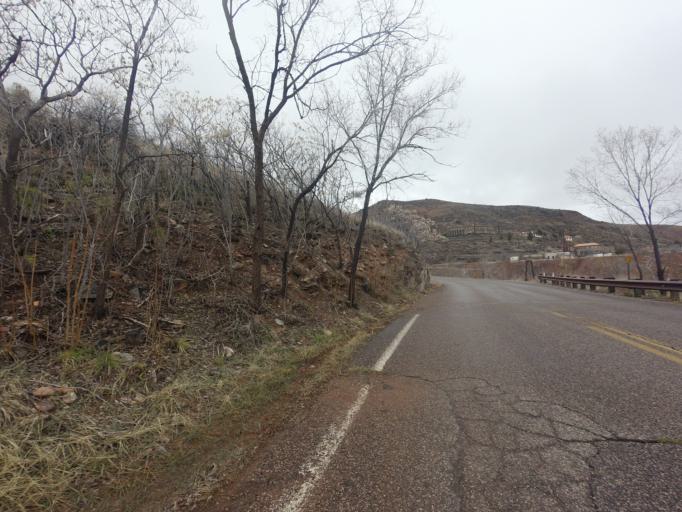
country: US
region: Arizona
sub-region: Yavapai County
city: Clarkdale
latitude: 34.7514
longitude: -112.1130
